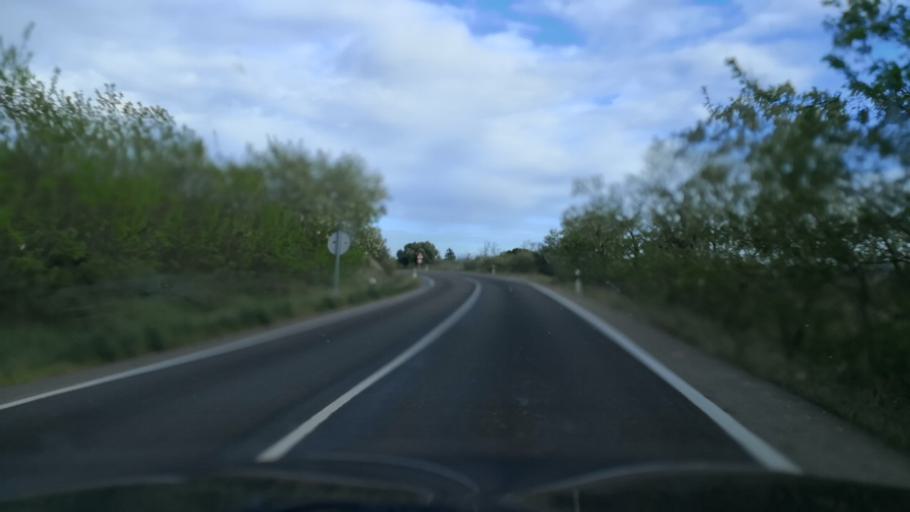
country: ES
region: Extremadura
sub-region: Provincia de Caceres
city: Coria
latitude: 40.0072
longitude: -6.5586
